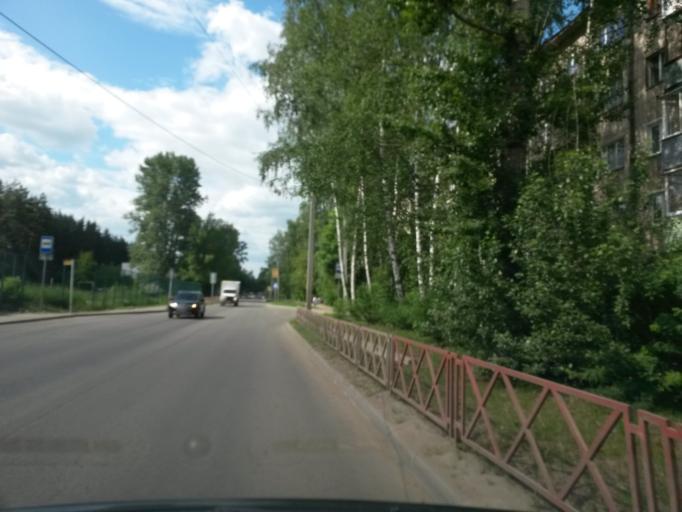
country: RU
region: Jaroslavl
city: Yaroslavl
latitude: 57.6484
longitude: 39.9388
